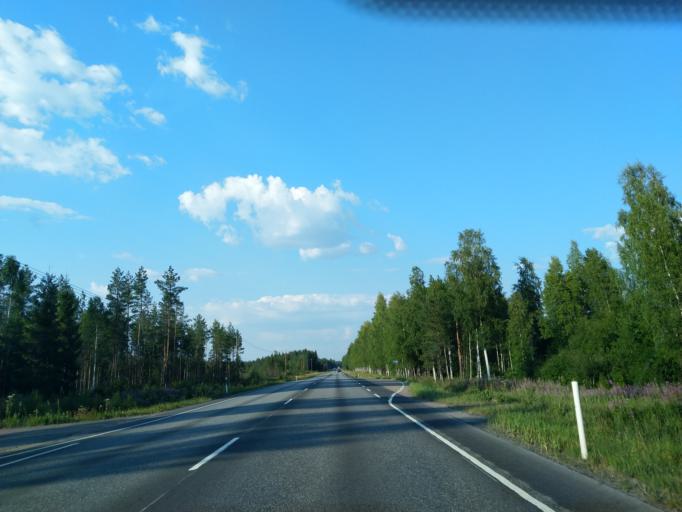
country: FI
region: Satakunta
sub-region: Pori
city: Pomarkku
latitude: 61.7339
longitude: 22.0778
